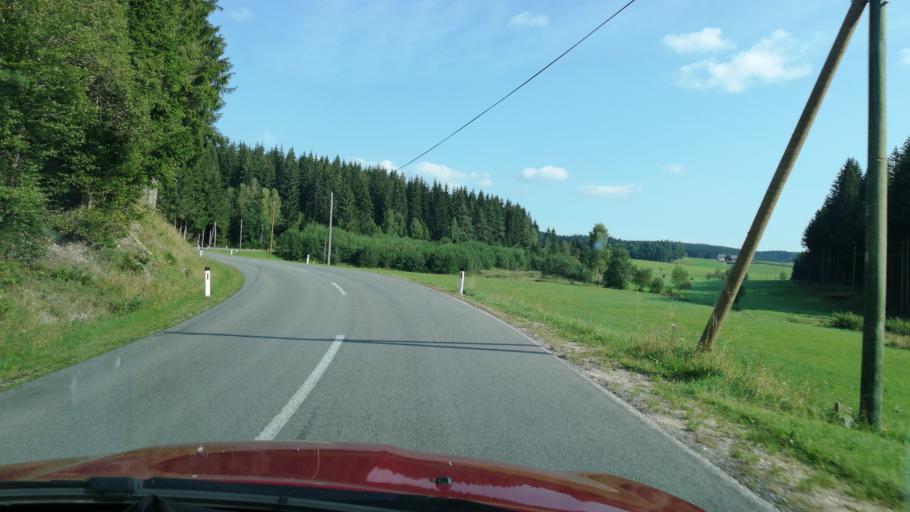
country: AT
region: Lower Austria
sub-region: Politischer Bezirk Zwettl
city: Langschlag
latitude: 48.4843
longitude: 14.8059
